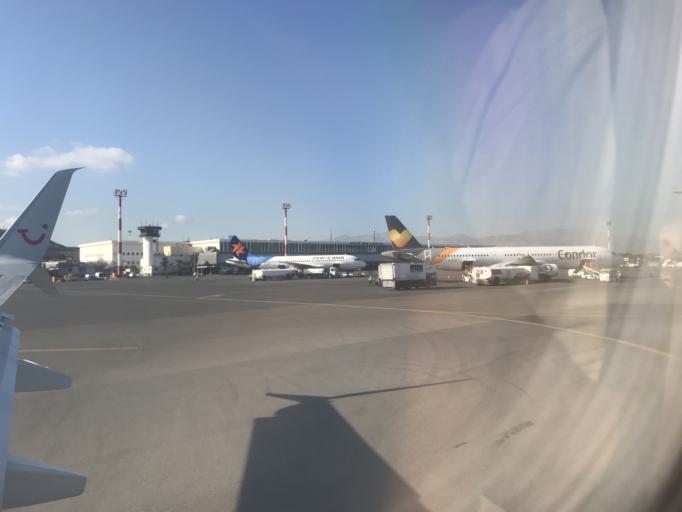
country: GR
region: Crete
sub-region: Nomos Irakleiou
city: Nea Alikarnassos
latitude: 35.3390
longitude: 25.1766
